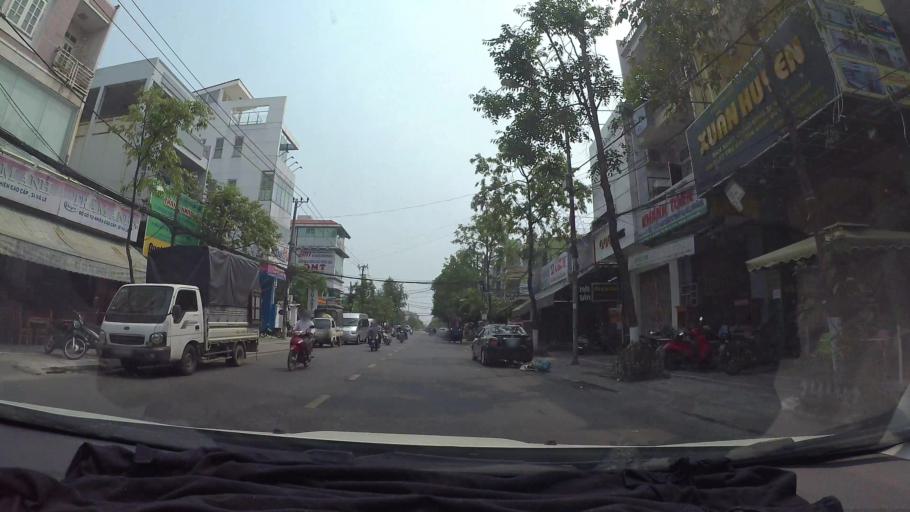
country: VN
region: Da Nang
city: Son Tra
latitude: 16.0505
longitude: 108.2206
